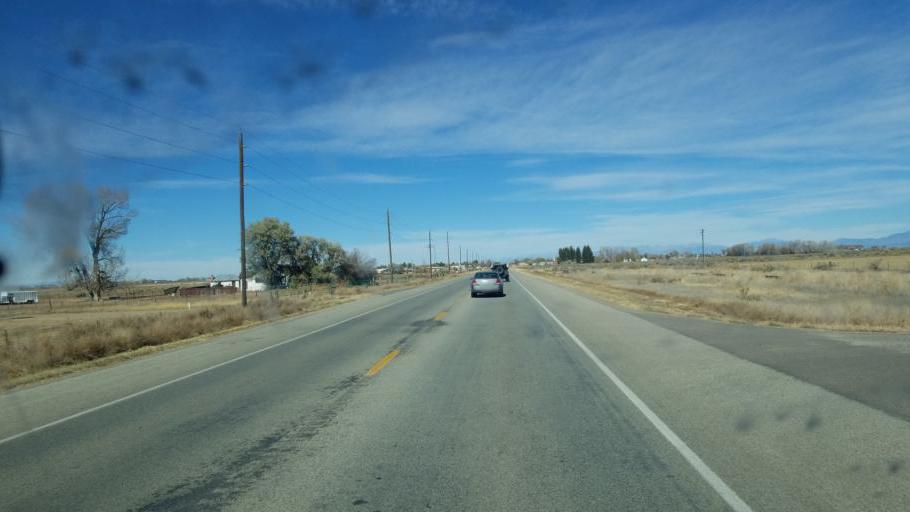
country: US
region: Colorado
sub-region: Conejos County
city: Conejos
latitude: 37.2524
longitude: -105.9671
